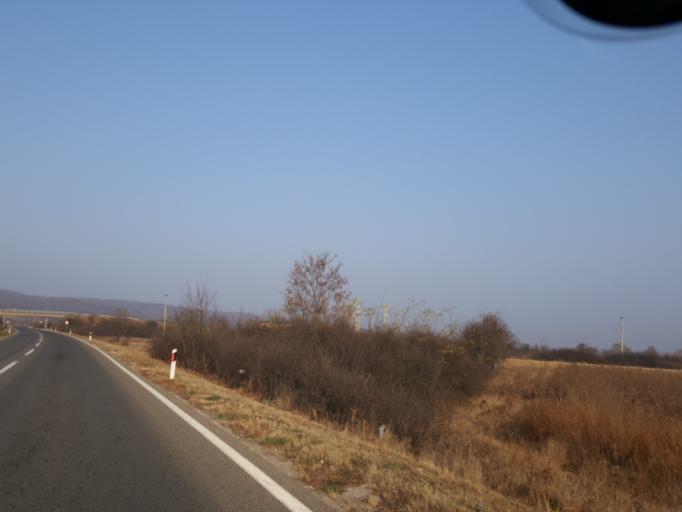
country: RS
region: Central Serbia
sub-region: Jablanicki Okrug
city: Leskovac
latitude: 42.9376
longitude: 22.0052
